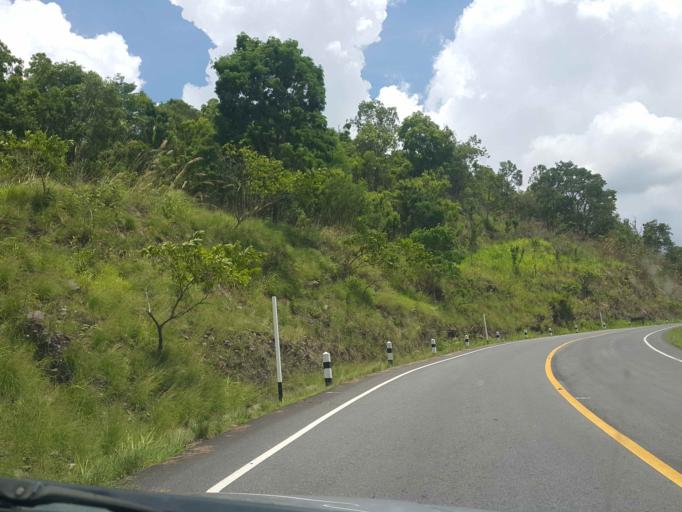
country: TH
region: Phayao
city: Chiang Muan
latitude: 18.8398
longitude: 100.3528
